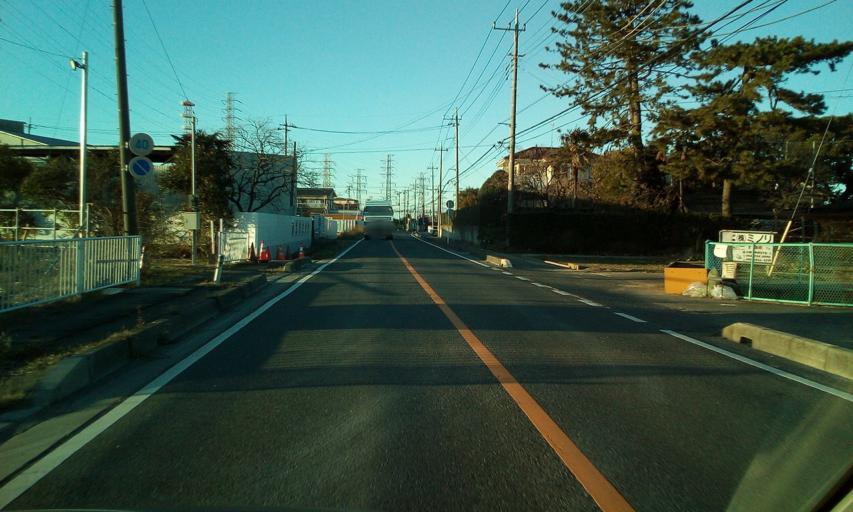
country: JP
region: Chiba
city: Nagareyama
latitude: 35.8649
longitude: 139.8738
